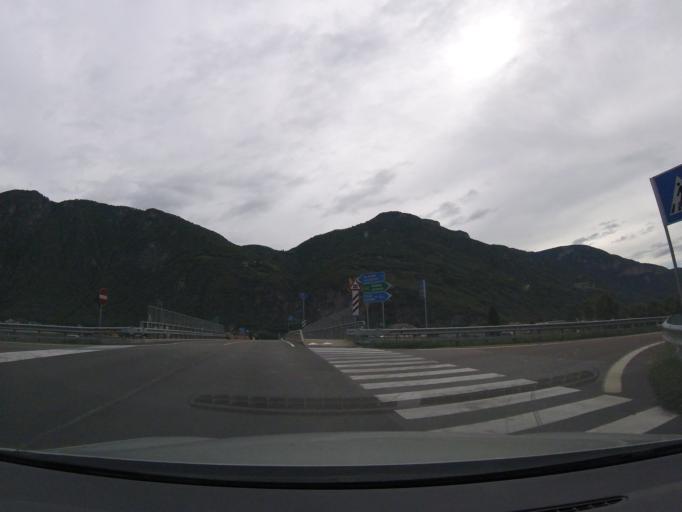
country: IT
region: Trentino-Alto Adige
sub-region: Bolzano
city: Nalles
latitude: 46.5551
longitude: 11.2166
